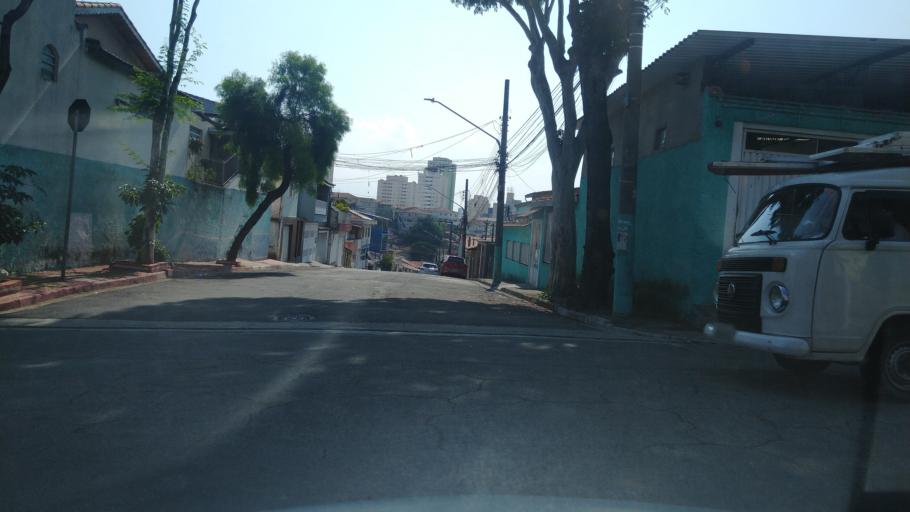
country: BR
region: Sao Paulo
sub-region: Sao Paulo
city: Sao Paulo
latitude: -23.4902
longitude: -46.6012
